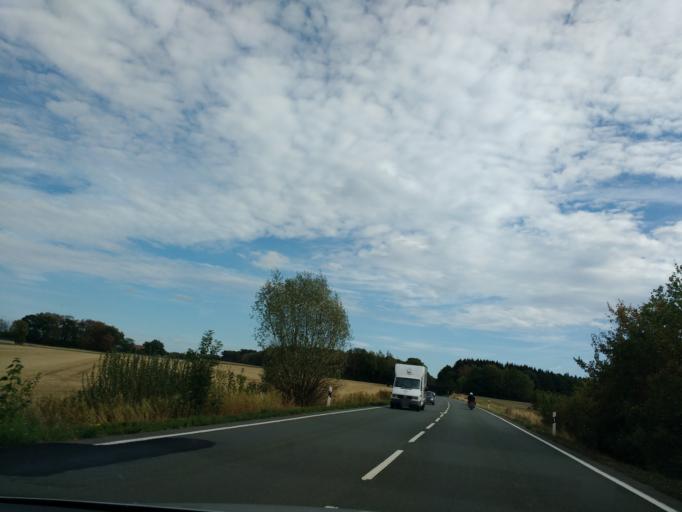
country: DE
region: North Rhine-Westphalia
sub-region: Regierungsbezirk Arnsberg
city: Anrochte
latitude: 51.5419
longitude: 8.3121
